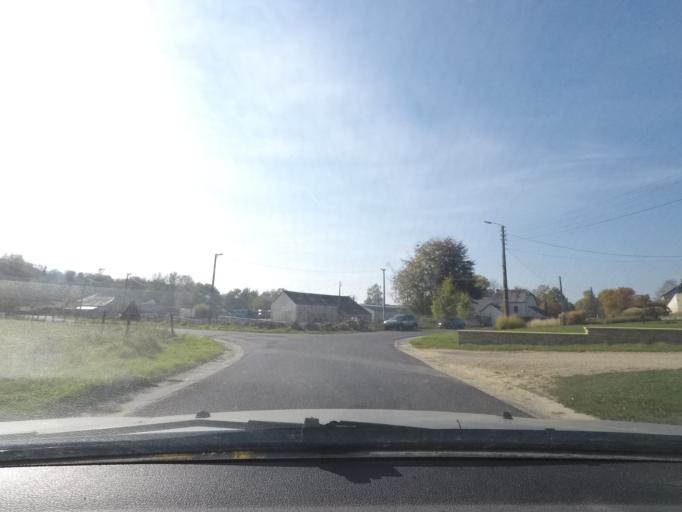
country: BE
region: Wallonia
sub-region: Province du Luxembourg
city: Tintigny
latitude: 49.6921
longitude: 5.4526
